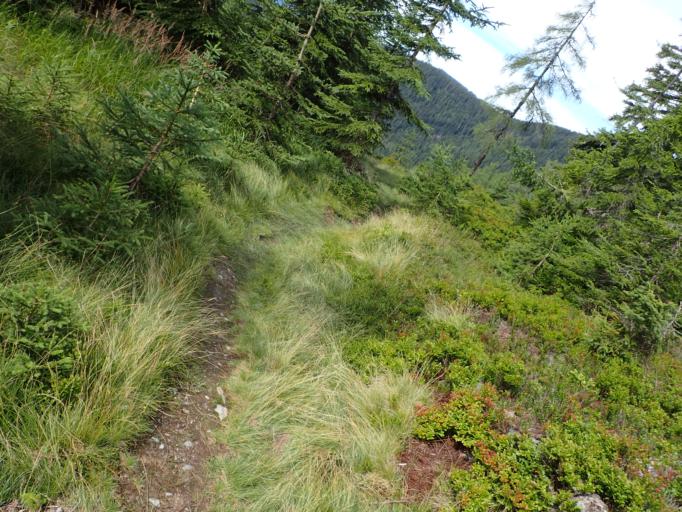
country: AT
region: Salzburg
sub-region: Politischer Bezirk Sankt Johann im Pongau
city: Radstadt
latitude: 47.4465
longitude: 13.4478
